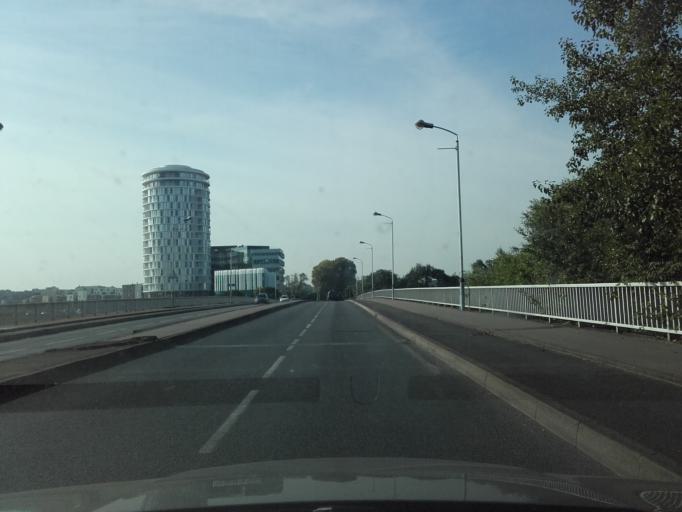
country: FR
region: Centre
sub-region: Departement d'Indre-et-Loire
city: Tours
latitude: 47.3733
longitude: 0.6784
